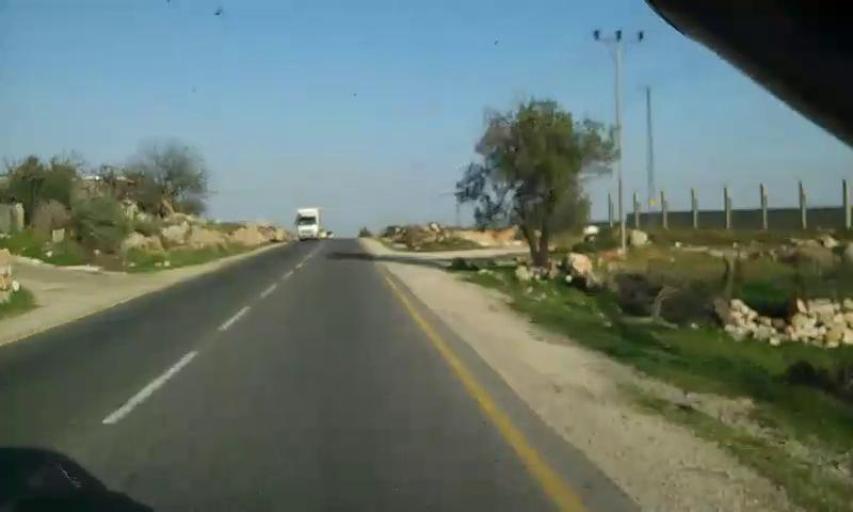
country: PS
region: West Bank
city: Jurat ash Sham`ah
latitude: 31.6478
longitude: 35.1740
